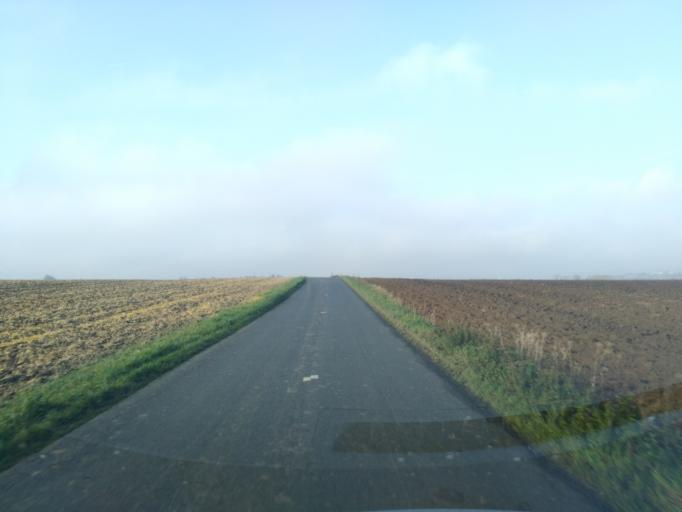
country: FR
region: Ile-de-France
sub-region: Departement des Yvelines
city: Saint-Germain-de-la-Grange
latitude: 48.8295
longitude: 1.9161
